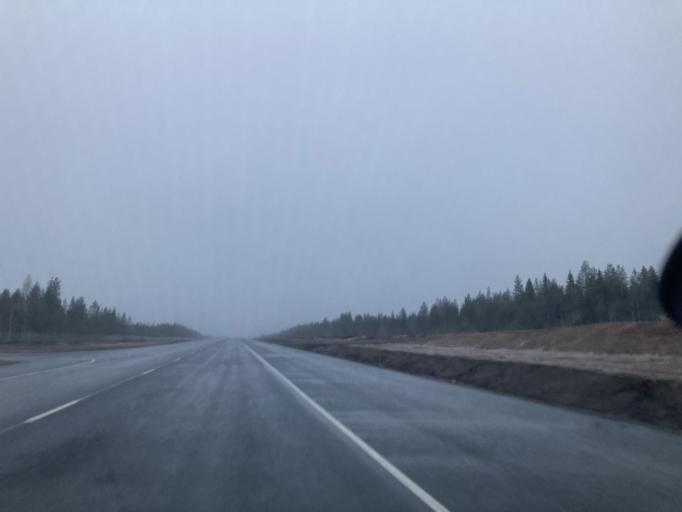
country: FI
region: Lapland
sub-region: Rovaniemi
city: Rovaniemi
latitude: 66.5789
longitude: 25.7997
